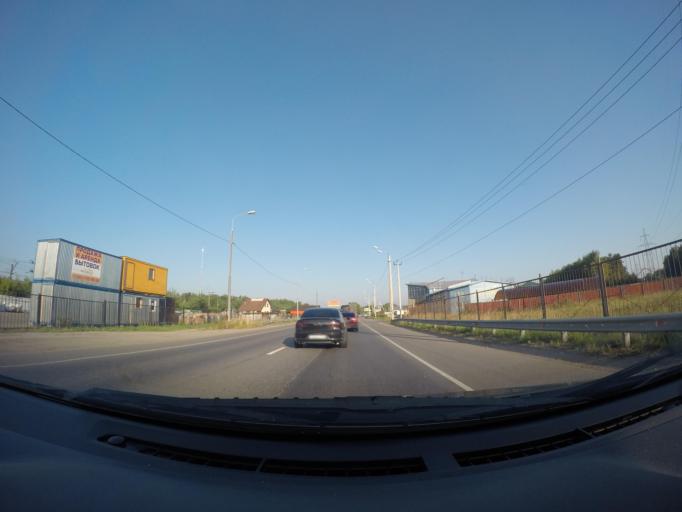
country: RU
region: Moskovskaya
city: Kratovo
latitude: 55.6409
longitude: 38.1624
